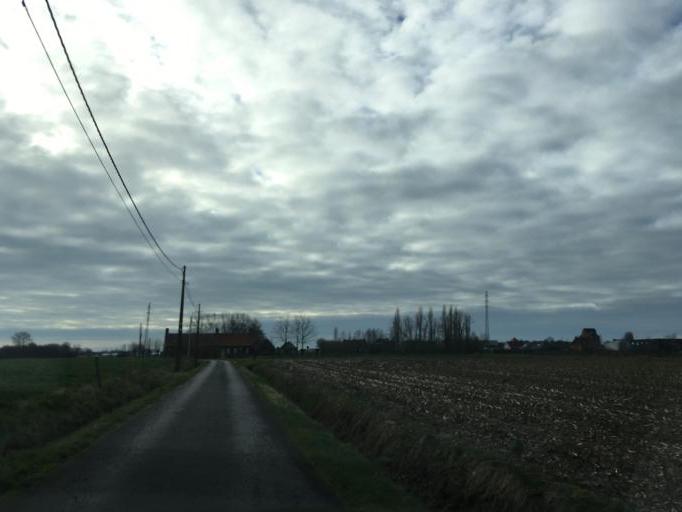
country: BE
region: Flanders
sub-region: Provincie West-Vlaanderen
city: Roeselare
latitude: 50.9074
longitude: 3.1464
